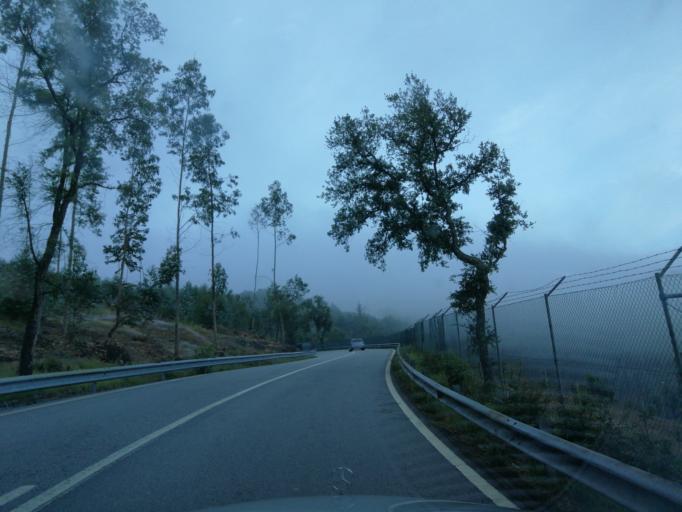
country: PT
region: Braga
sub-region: Braga
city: Braga
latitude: 41.5261
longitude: -8.3891
